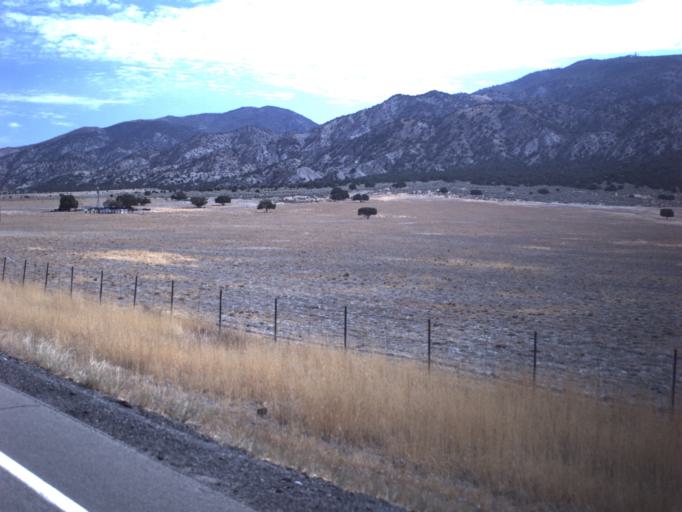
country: US
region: Utah
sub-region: Juab County
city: Nephi
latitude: 39.4863
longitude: -111.8856
